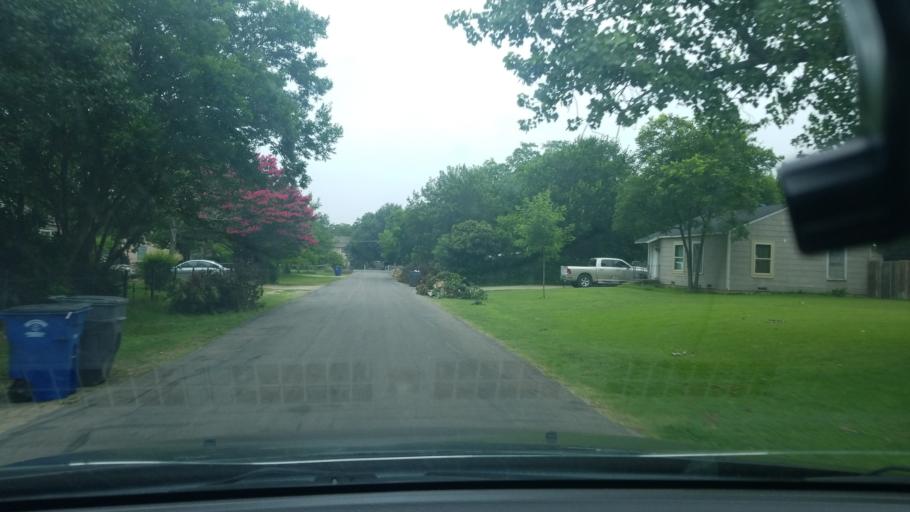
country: US
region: Texas
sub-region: Dallas County
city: Balch Springs
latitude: 32.7558
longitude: -96.6757
